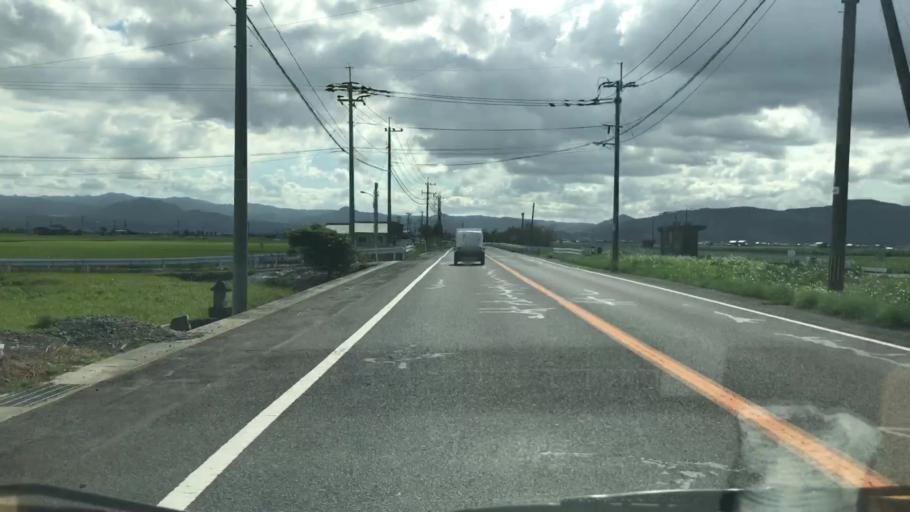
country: JP
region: Saga Prefecture
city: Kashima
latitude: 33.1577
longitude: 130.1617
